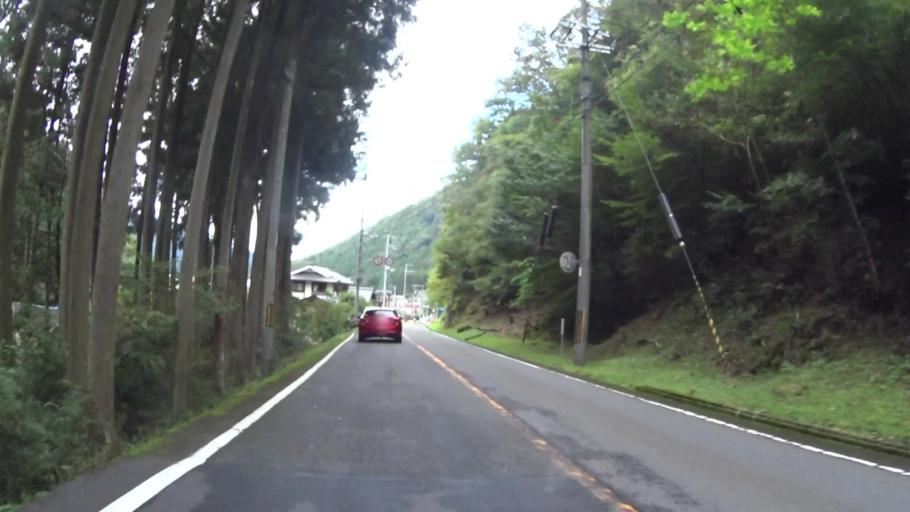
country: JP
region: Kyoto
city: Kameoka
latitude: 35.2773
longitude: 135.5588
